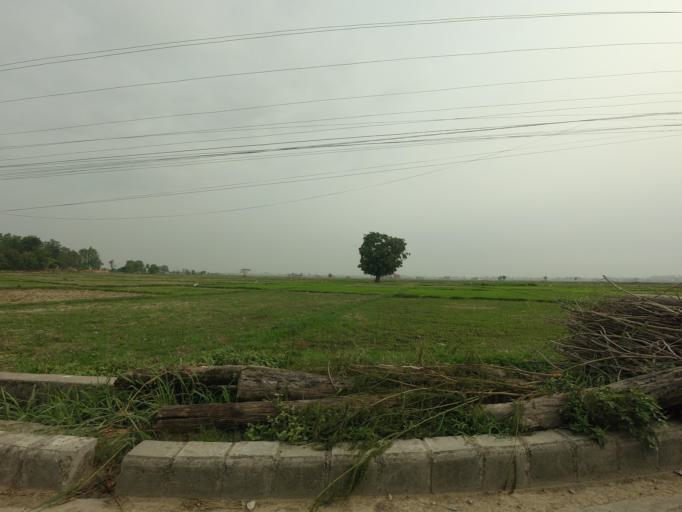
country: NP
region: Western Region
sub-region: Lumbini Zone
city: Bhairahawa
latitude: 27.4892
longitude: 83.4326
